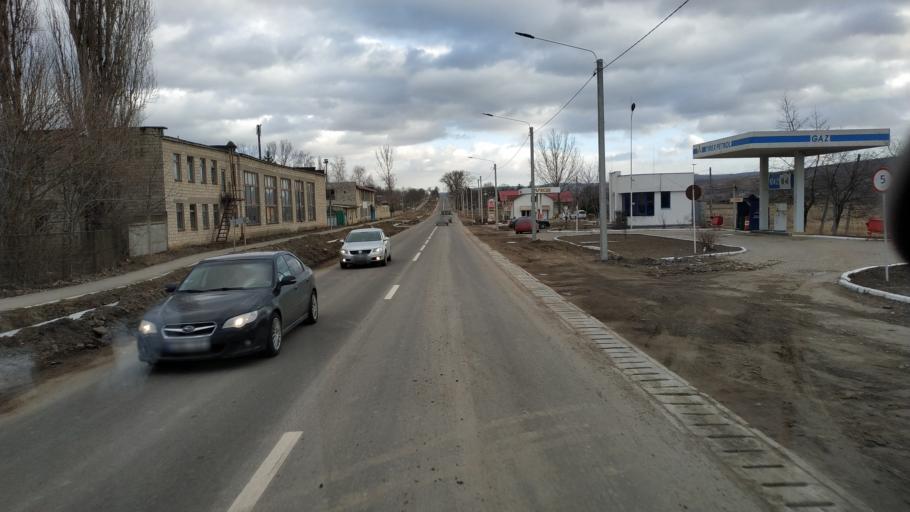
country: MD
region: Calarasi
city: Calarasi
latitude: 47.2810
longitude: 28.2077
